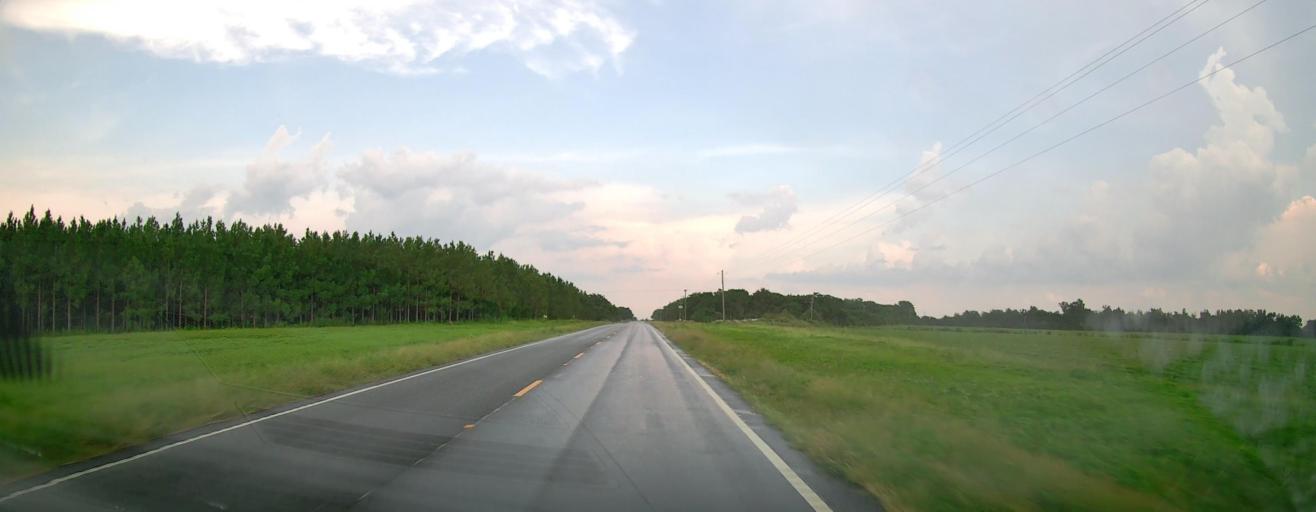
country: US
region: Georgia
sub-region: Dodge County
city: Chester
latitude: 32.5512
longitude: -83.1343
